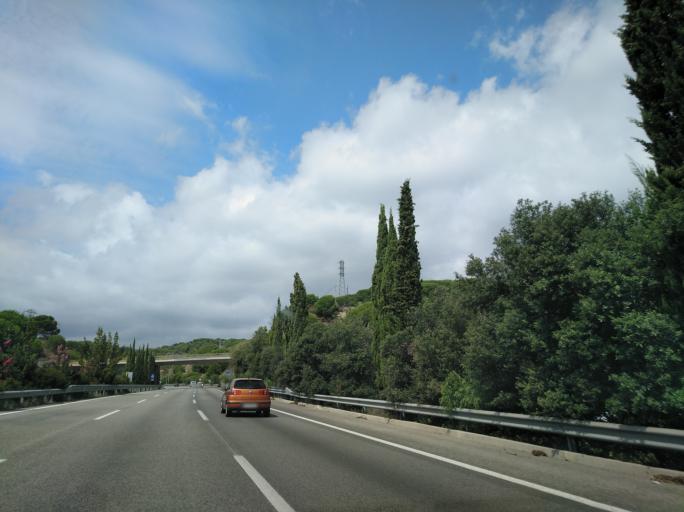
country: ES
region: Catalonia
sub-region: Provincia de Barcelona
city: Canet de Mar
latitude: 41.5998
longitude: 2.5848
